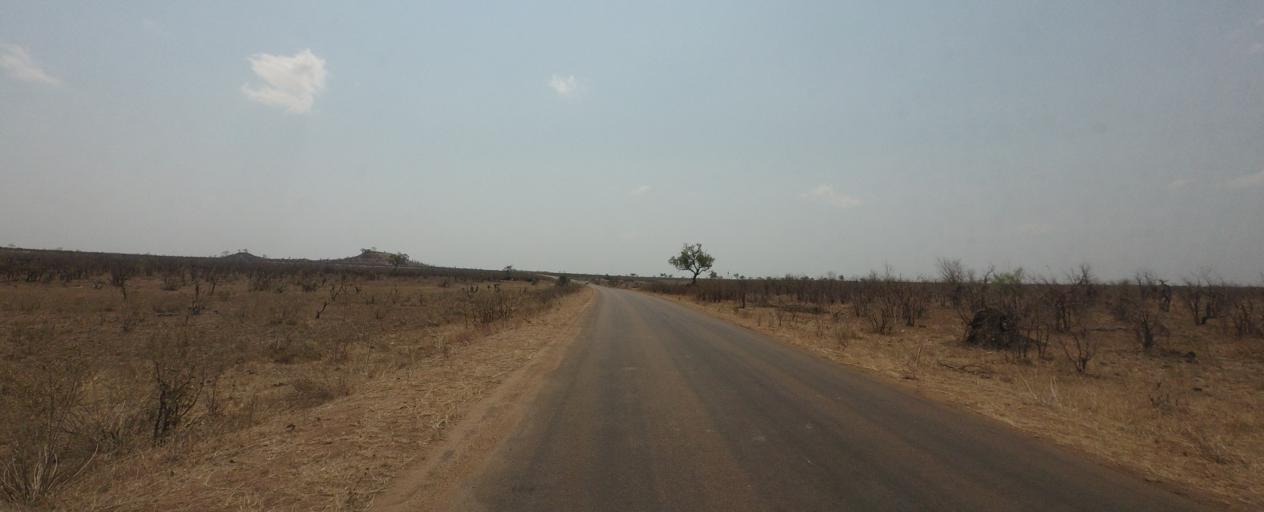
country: ZA
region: Limpopo
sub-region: Mopani District Municipality
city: Phalaborwa
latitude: -23.5013
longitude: 31.4028
